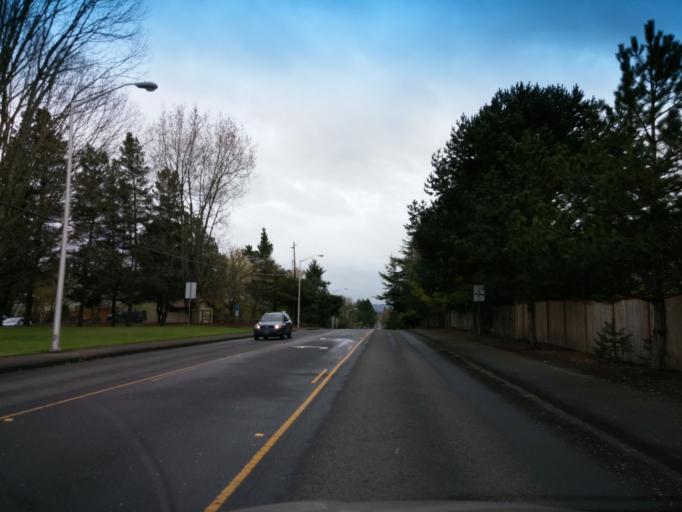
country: US
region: Oregon
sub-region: Washington County
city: Oak Hills
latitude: 45.5302
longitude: -122.8548
